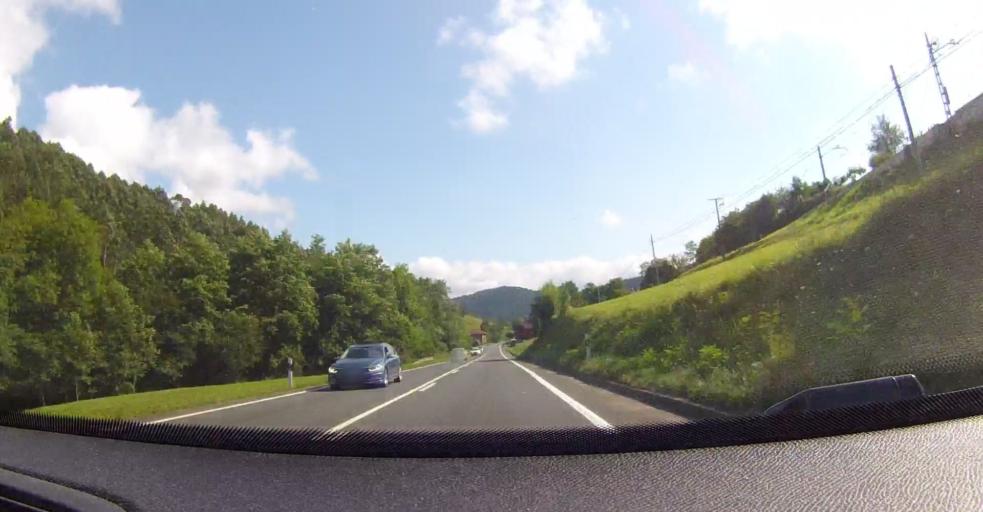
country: ES
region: Basque Country
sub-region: Bizkaia
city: Muxika
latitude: 43.2788
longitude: -2.6847
